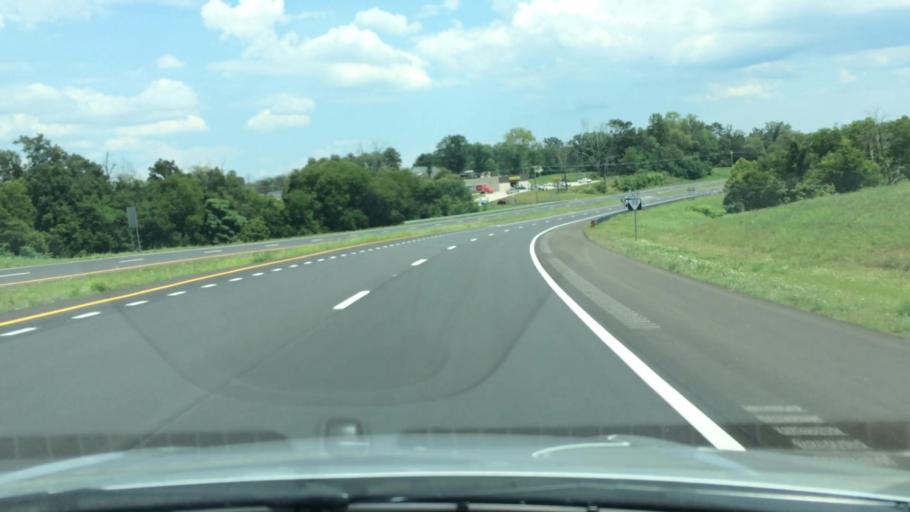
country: US
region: Tennessee
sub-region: Hamblen County
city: Morristown
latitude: 36.1823
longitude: -83.2375
